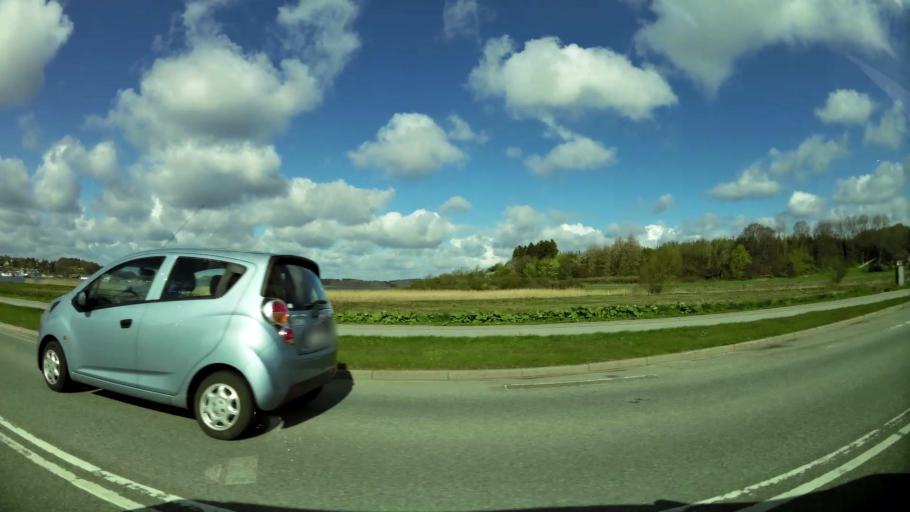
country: DK
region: North Denmark
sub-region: Mariagerfjord Kommune
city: Mariager
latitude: 56.6568
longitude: 9.9883
